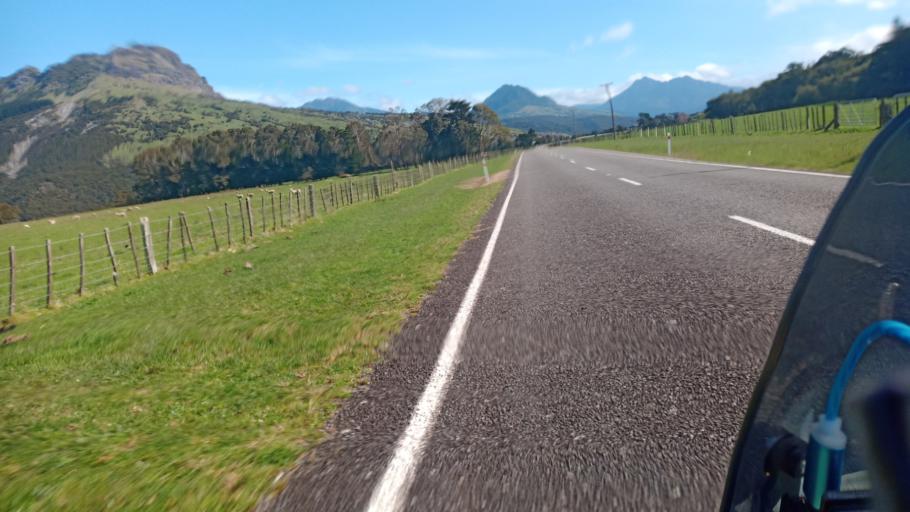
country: NZ
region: Gisborne
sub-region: Gisborne District
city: Gisborne
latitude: -37.8653
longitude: 178.2170
